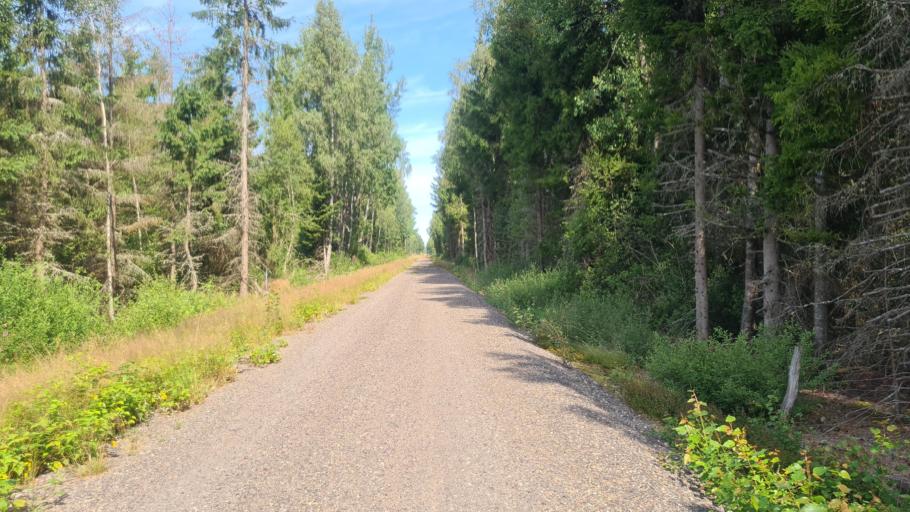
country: SE
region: Kronoberg
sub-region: Ljungby Kommun
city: Lagan
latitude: 56.9637
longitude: 13.9539
